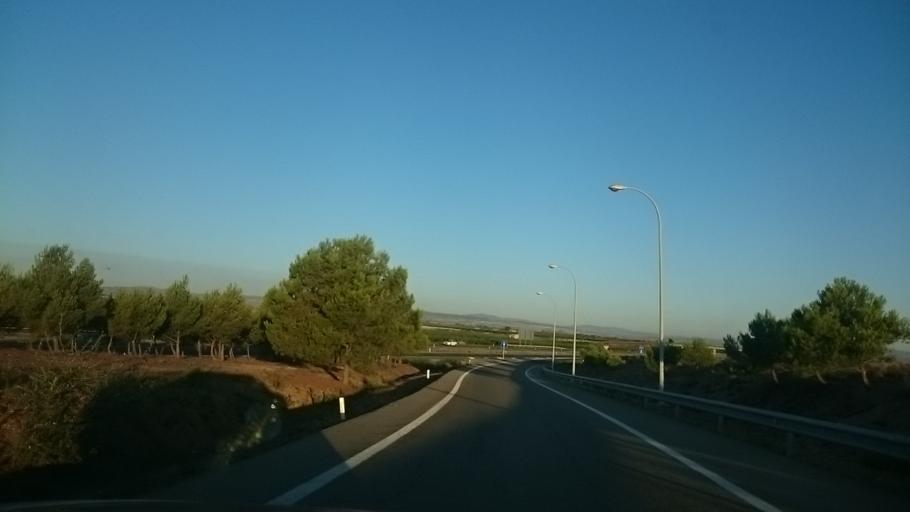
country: ES
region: Navarre
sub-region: Provincia de Navarra
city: Fontellas
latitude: 42.0148
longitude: -1.6039
